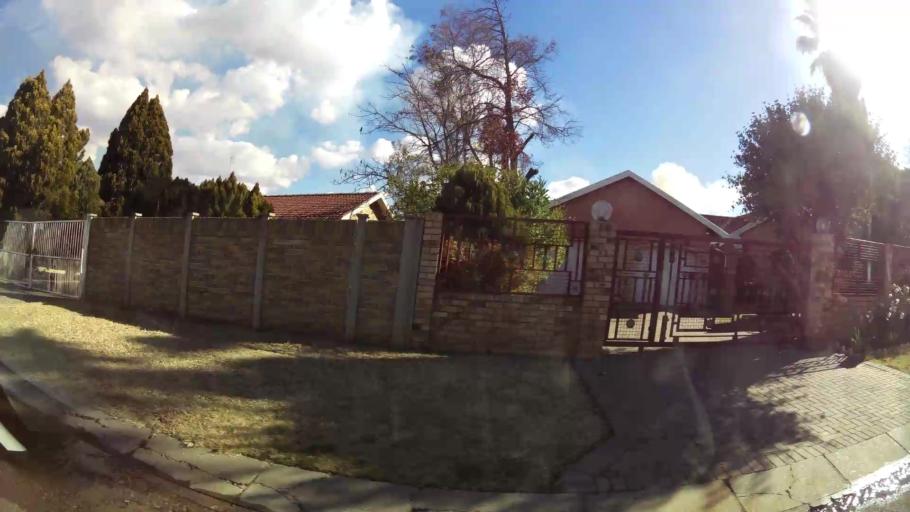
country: ZA
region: North-West
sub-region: Dr Kenneth Kaunda District Municipality
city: Klerksdorp
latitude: -26.8263
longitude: 26.6624
